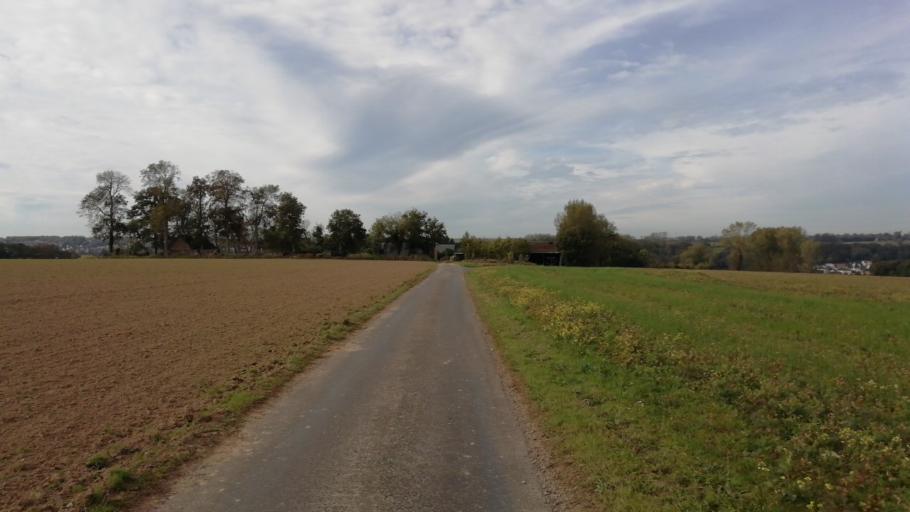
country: FR
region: Haute-Normandie
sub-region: Departement de la Seine-Maritime
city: Epouville
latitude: 49.5429
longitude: 0.2132
